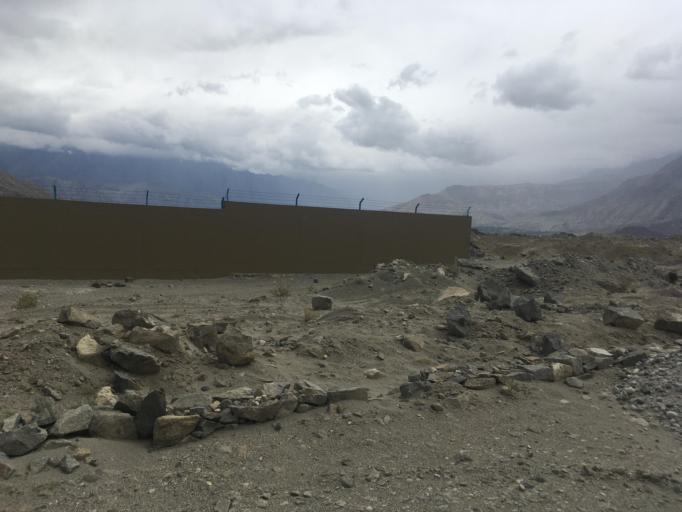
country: PK
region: Gilgit-Baltistan
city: Skardu
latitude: 35.3209
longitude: 75.6558
